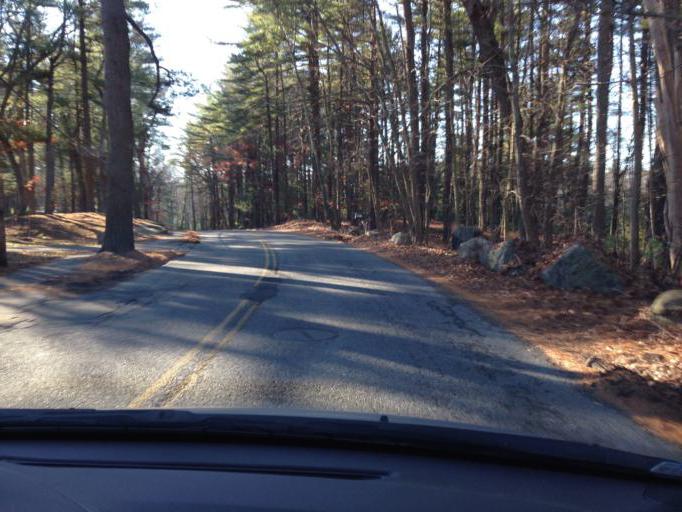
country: US
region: Massachusetts
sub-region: Middlesex County
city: Bedford
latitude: 42.5146
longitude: -71.2710
